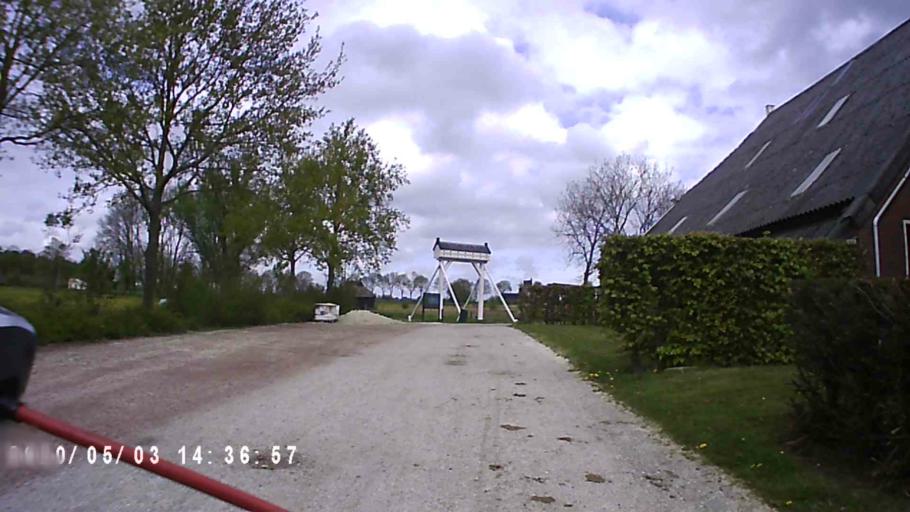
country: NL
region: Groningen
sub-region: Gemeente Zuidhorn
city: Oldehove
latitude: 53.3603
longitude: 6.3982
